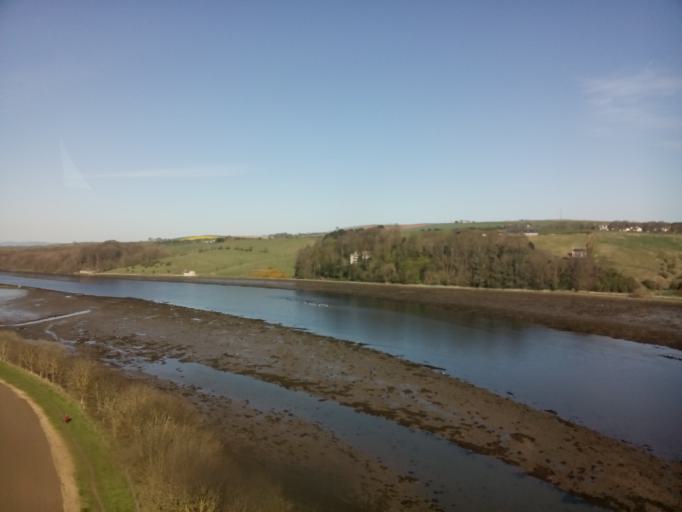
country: GB
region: England
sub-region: Northumberland
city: Berwick-Upon-Tweed
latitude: 55.7713
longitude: -2.0148
